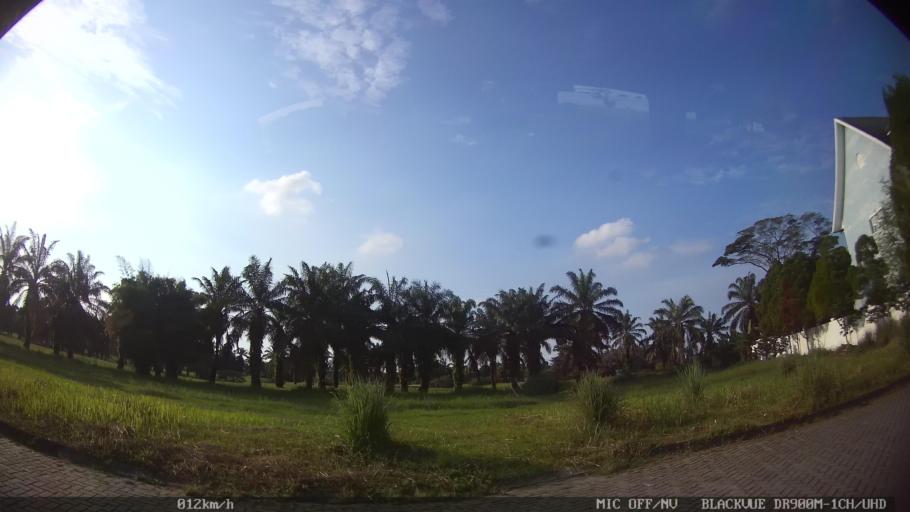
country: ID
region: North Sumatra
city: Medan
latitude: 3.6225
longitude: 98.6488
